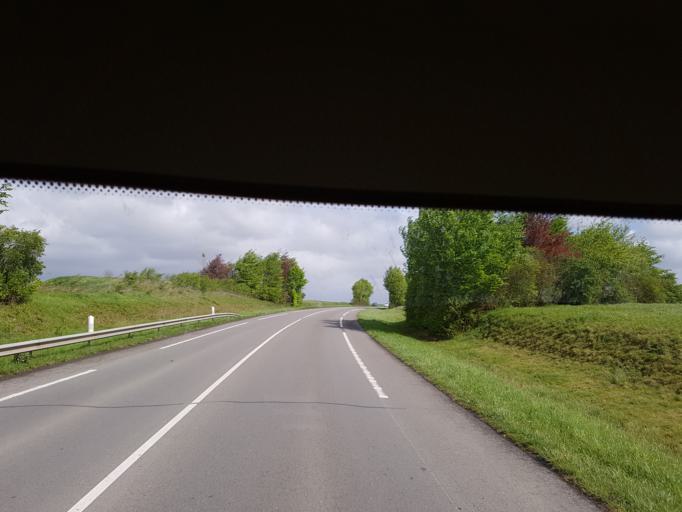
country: FR
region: Nord-Pas-de-Calais
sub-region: Departement du Nord
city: Raillencourt-Sainte-Olle
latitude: 50.1876
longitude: 3.1885
